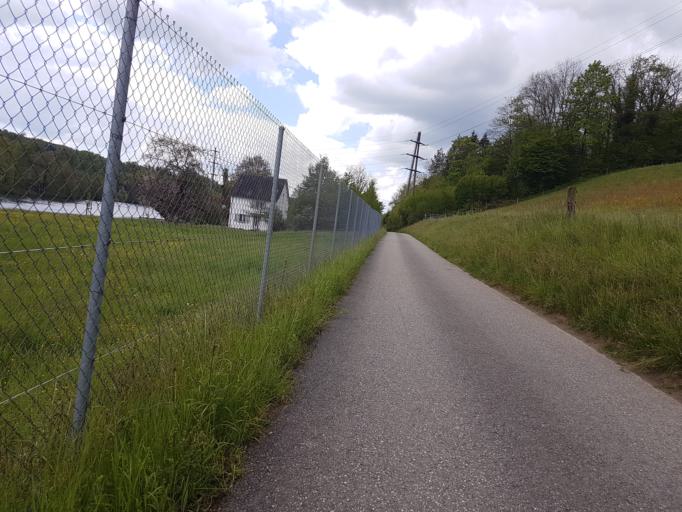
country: CH
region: Solothurn
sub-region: Bezirk Gaeu
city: Wolfwil
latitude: 47.2571
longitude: 7.7839
